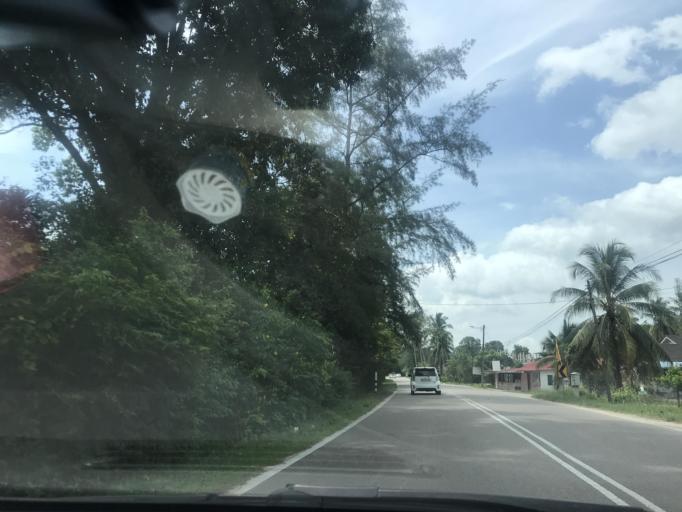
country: MY
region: Kelantan
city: Tumpat
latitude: 6.2156
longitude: 102.1249
